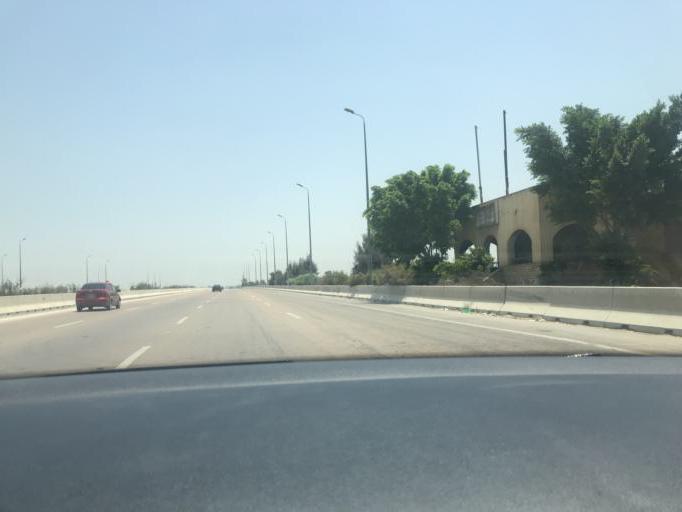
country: EG
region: Al Buhayrah
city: Abu al Matamir
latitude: 30.7296
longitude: 30.0181
